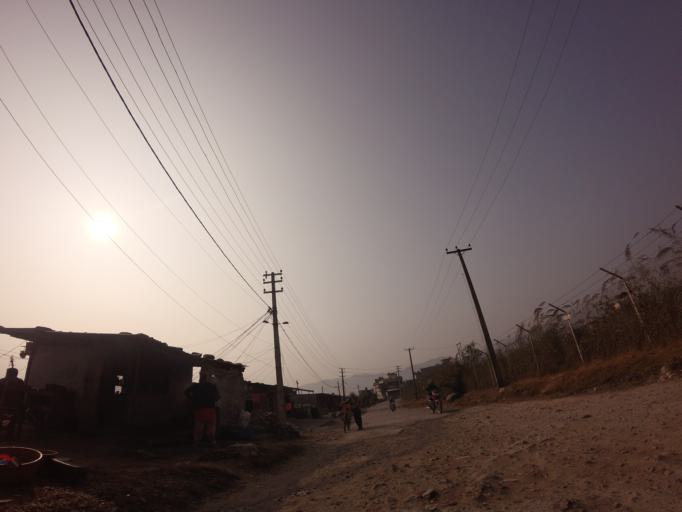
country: NP
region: Western Region
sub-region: Gandaki Zone
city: Pokhara
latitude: 28.2010
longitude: 83.9852
